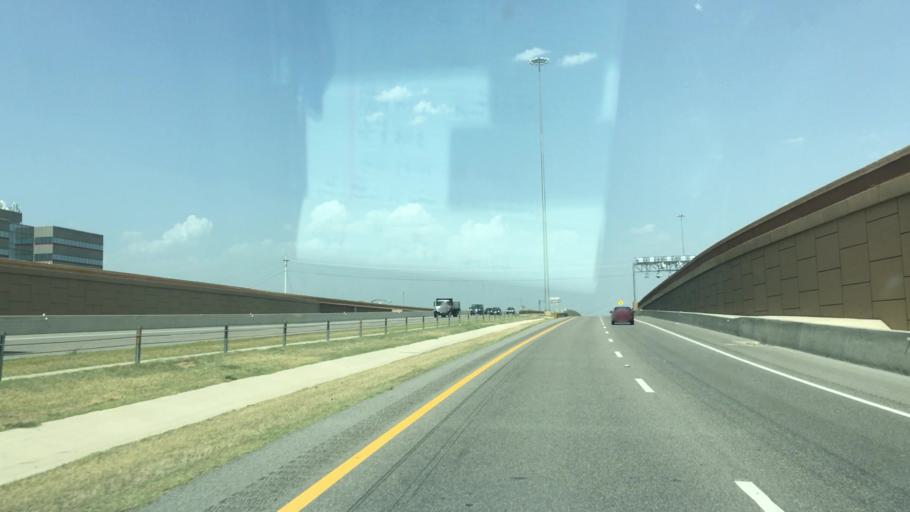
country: US
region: Texas
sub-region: Tarrant County
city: Hurst
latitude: 32.8381
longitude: -97.1923
